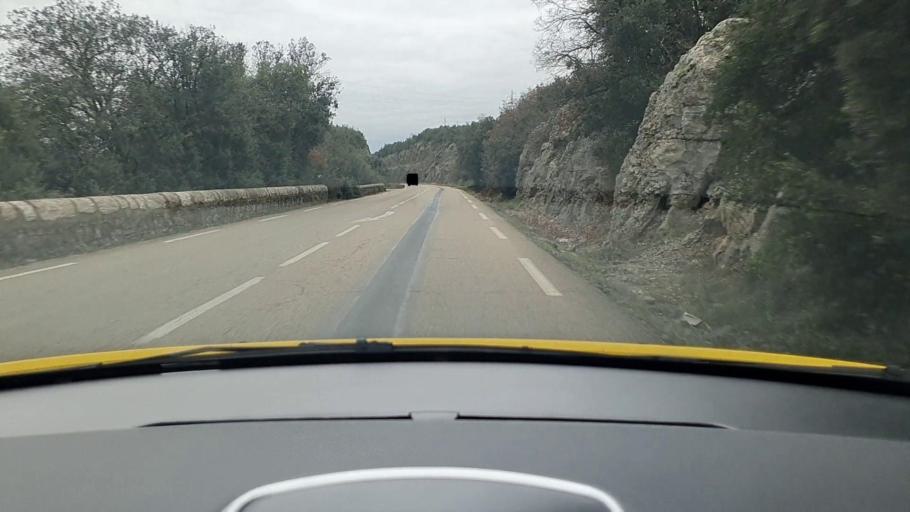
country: FR
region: Languedoc-Roussillon
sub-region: Departement du Gard
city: Saint-Martin-de-Valgalgues
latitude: 44.1774
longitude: 4.0816
